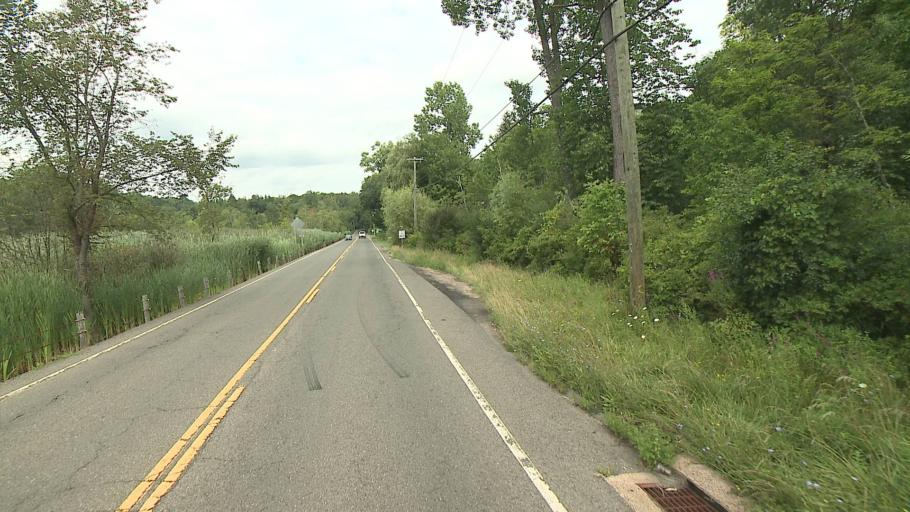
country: US
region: Connecticut
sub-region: Fairfield County
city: Sherman
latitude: 41.6393
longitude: -73.4990
